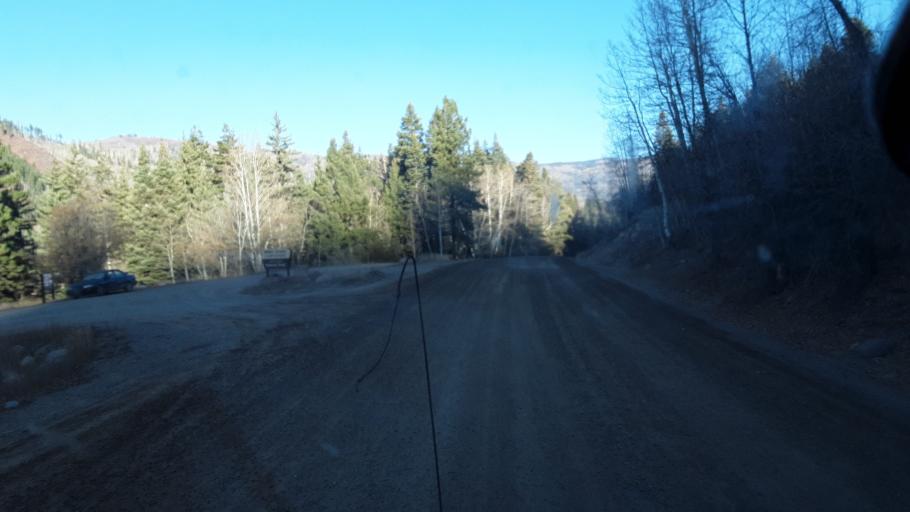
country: US
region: Colorado
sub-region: La Plata County
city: Bayfield
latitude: 37.4059
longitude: -107.6605
